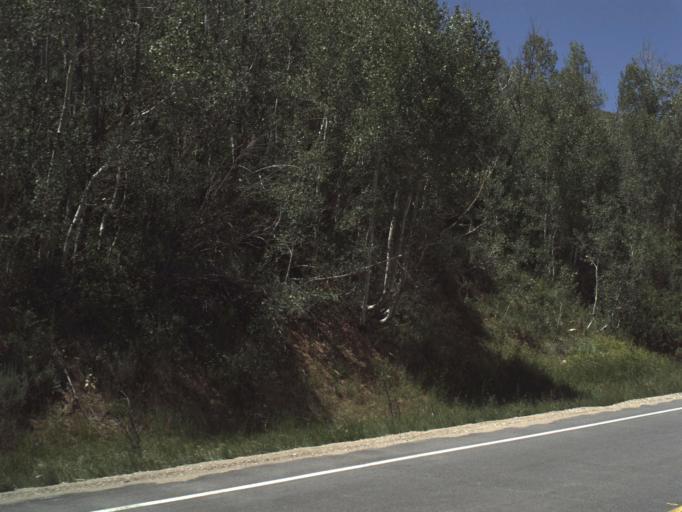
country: US
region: Utah
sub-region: Weber County
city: Wolf Creek
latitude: 41.4019
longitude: -111.5988
